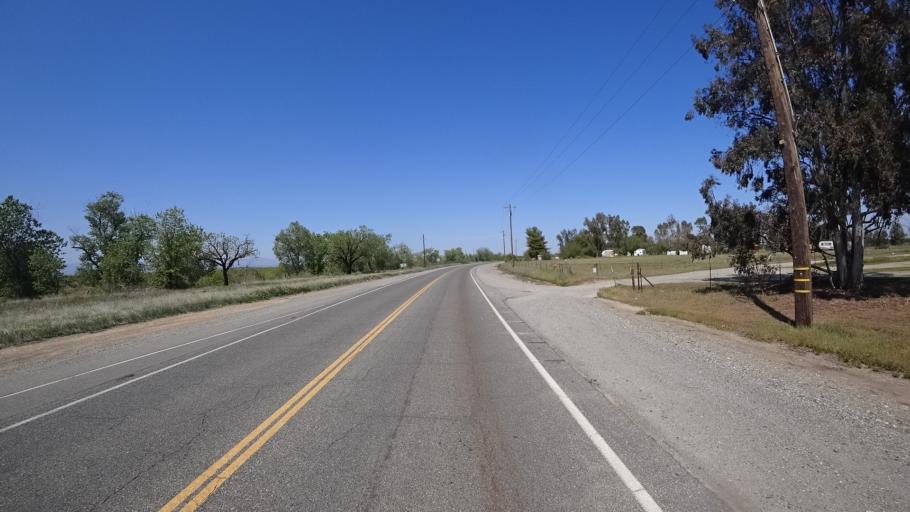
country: US
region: California
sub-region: Glenn County
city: Willows
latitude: 39.6248
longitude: -122.1959
